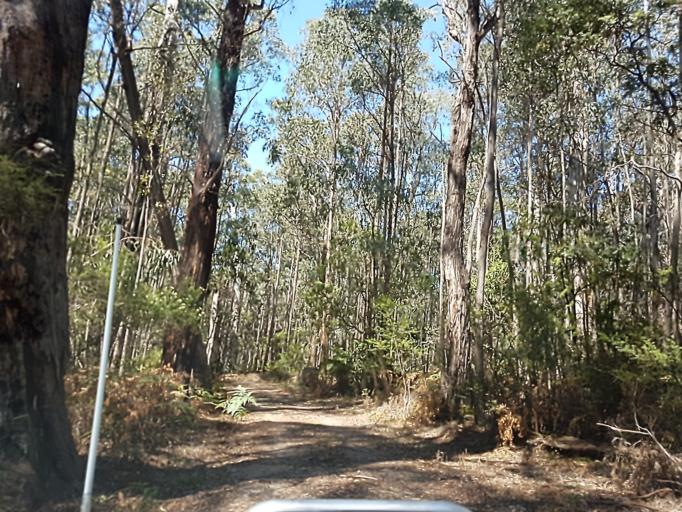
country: AU
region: Victoria
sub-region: East Gippsland
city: Lakes Entrance
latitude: -37.2923
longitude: 148.3247
